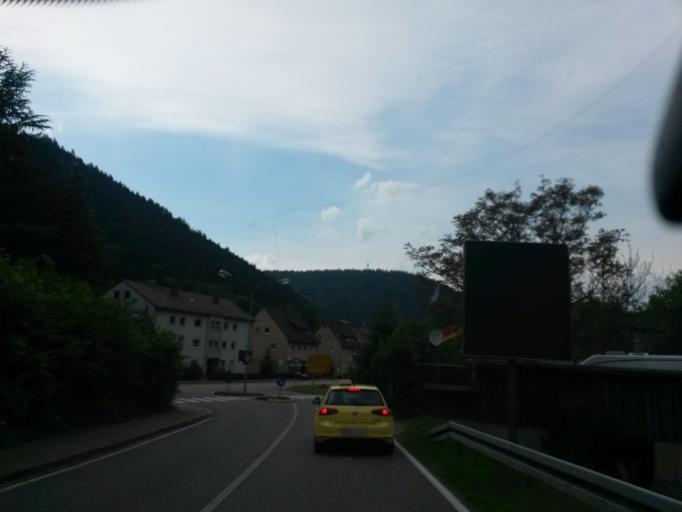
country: DE
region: Baden-Wuerttemberg
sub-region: Karlsruhe Region
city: Hofen an der Enz
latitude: 48.7701
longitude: 8.5853
